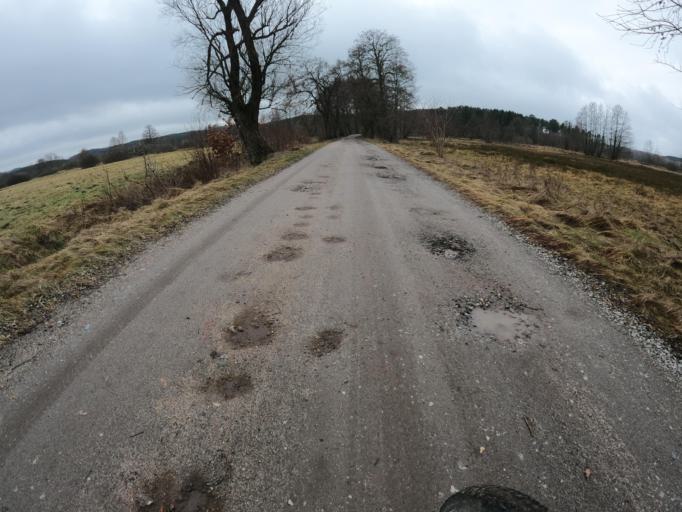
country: PL
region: West Pomeranian Voivodeship
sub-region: Powiat slawienski
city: Slawno
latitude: 54.2539
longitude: 16.6444
